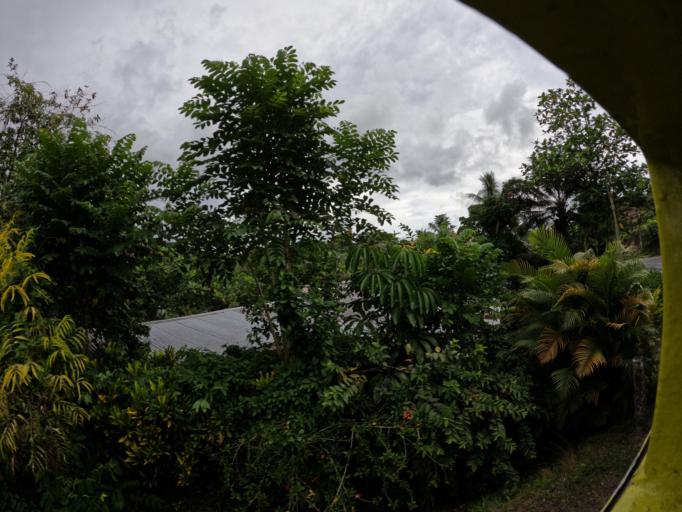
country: FJ
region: Central
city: Suva
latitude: -18.0736
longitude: 178.4612
